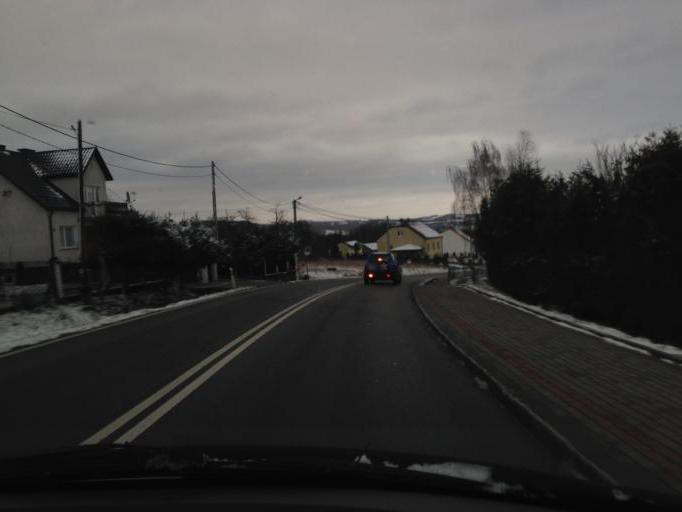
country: PL
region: Lesser Poland Voivodeship
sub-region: Powiat tarnowski
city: Gromnik
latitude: 49.8421
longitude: 20.9483
